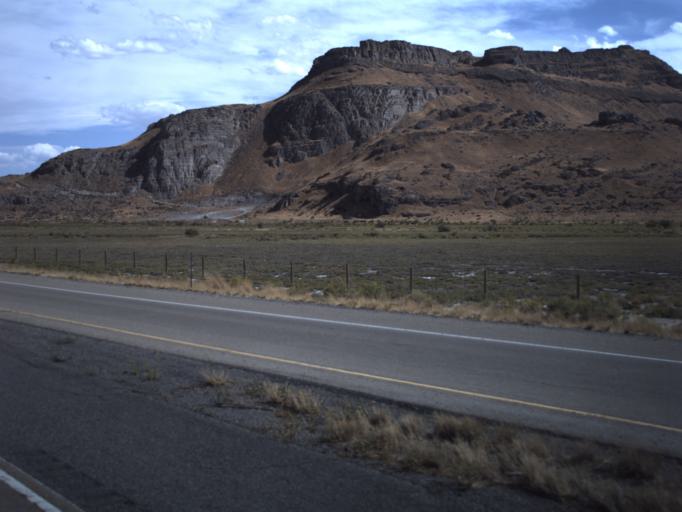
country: US
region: Utah
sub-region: Tooele County
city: Grantsville
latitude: 40.7452
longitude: -112.6484
